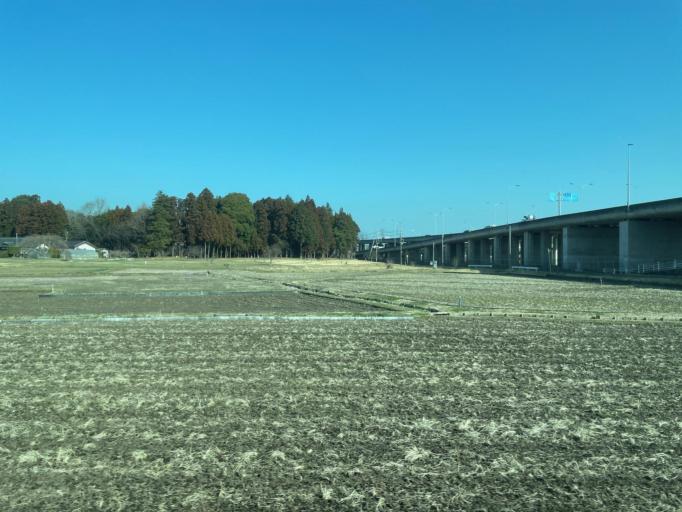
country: JP
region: Ibaraki
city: Mito-shi
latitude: 36.3800
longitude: 140.4011
